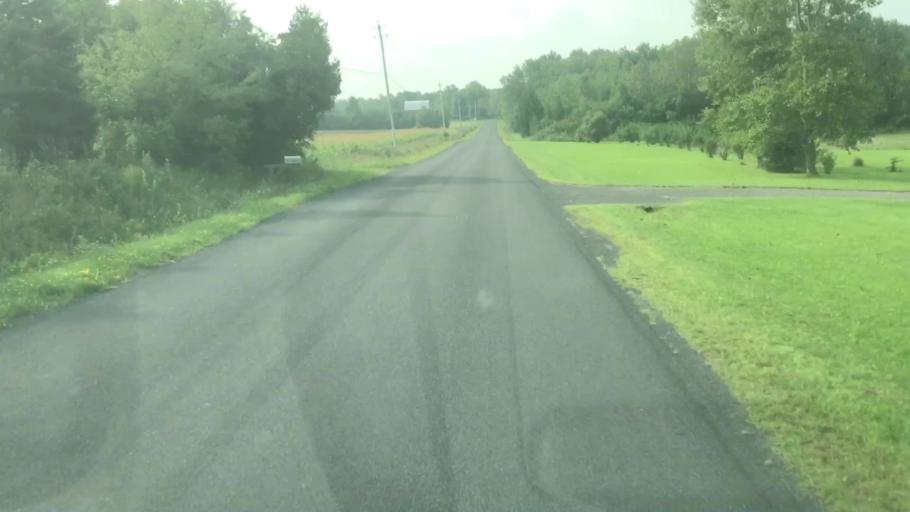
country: US
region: New York
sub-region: Onondaga County
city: Skaneateles
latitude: 42.9178
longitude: -76.4565
